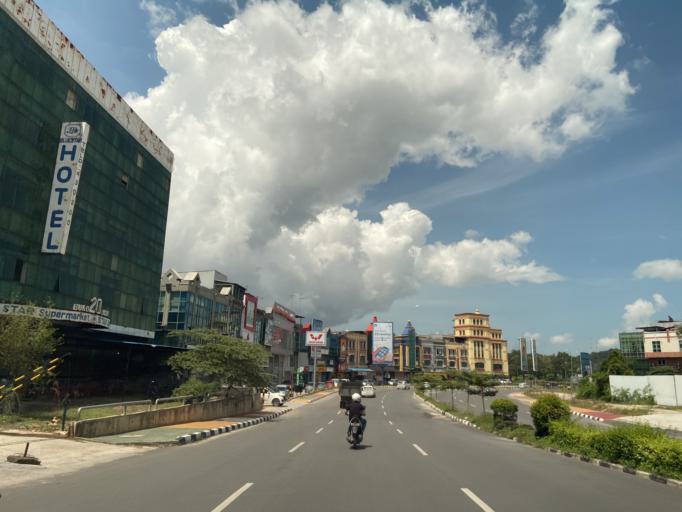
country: SG
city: Singapore
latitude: 1.1339
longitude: 104.0174
